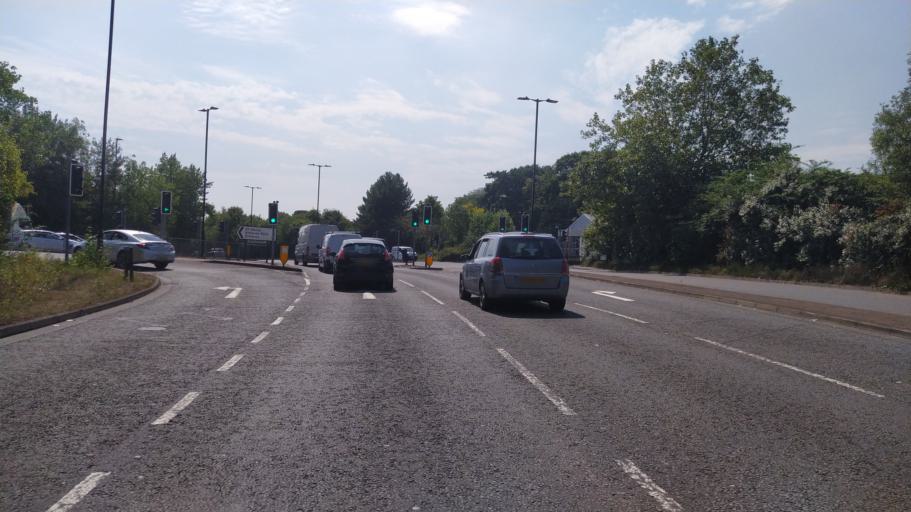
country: GB
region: England
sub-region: Southampton
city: Southampton
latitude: 50.9255
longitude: -1.3867
